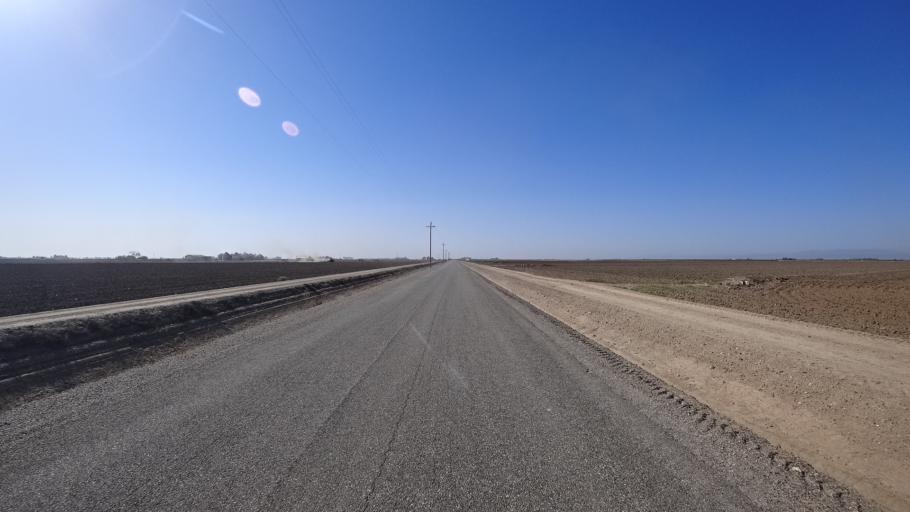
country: US
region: California
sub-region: Glenn County
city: Willows
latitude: 39.6039
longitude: -122.1167
